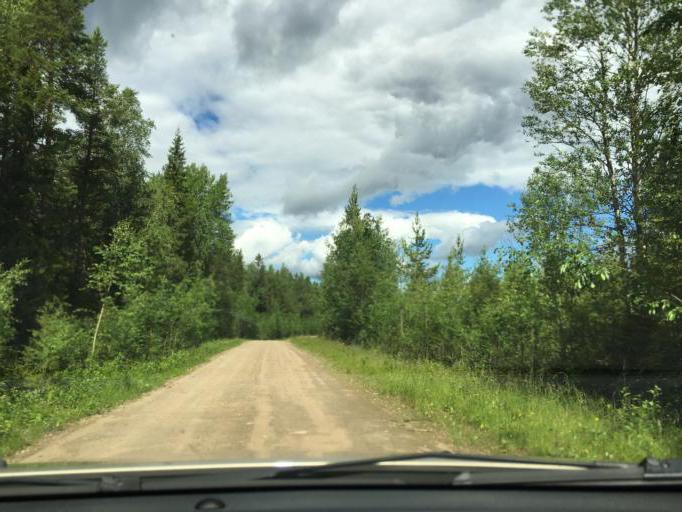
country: SE
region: Norrbotten
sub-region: Overkalix Kommun
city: OEverkalix
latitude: 66.1624
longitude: 22.8541
